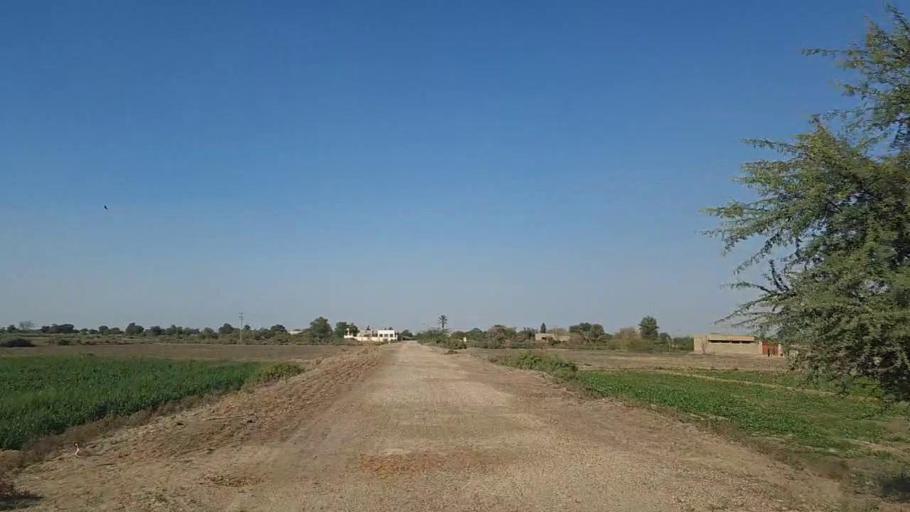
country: PK
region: Sindh
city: Shahpur Chakar
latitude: 26.2199
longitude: 68.6348
